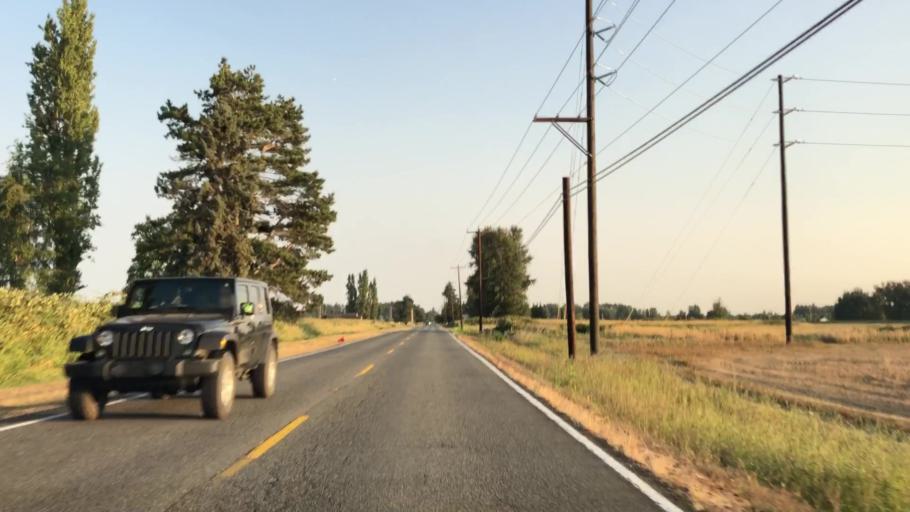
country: US
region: Washington
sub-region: Snohomish County
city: Smokey Point
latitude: 48.1417
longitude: -122.1617
